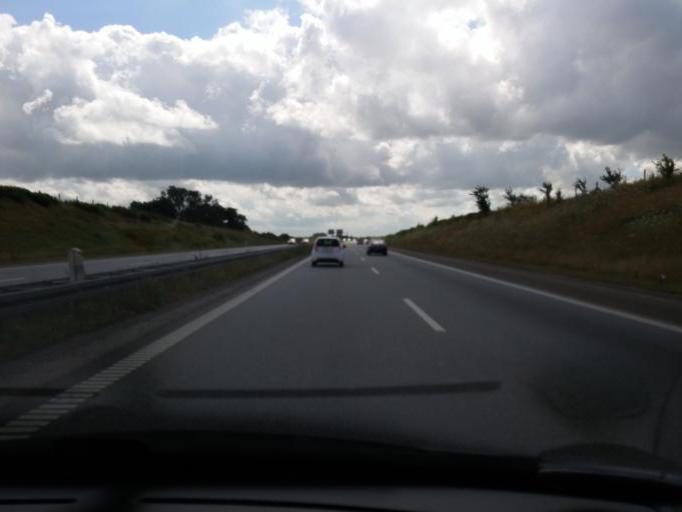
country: DK
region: South Denmark
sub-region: Odense Kommune
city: Hojby
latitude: 55.3338
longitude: 10.4506
